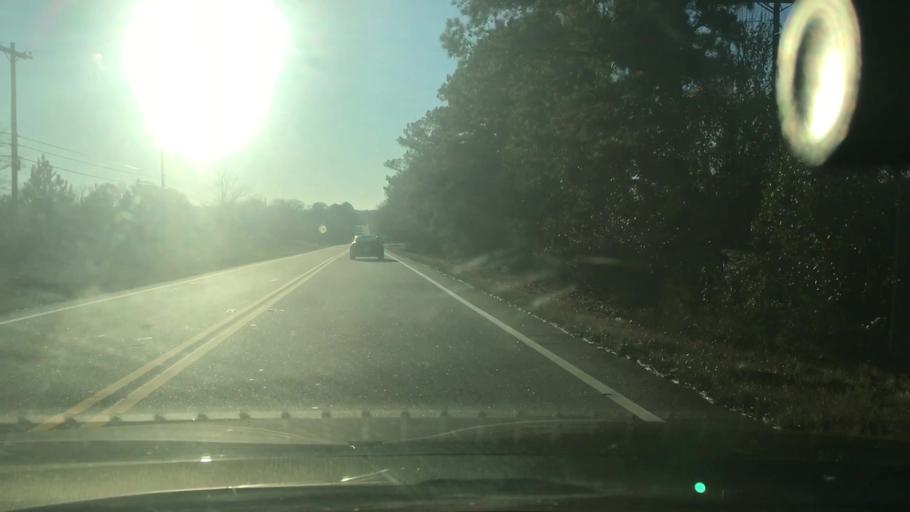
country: US
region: Georgia
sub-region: Coweta County
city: Senoia
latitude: 33.2729
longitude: -84.5295
